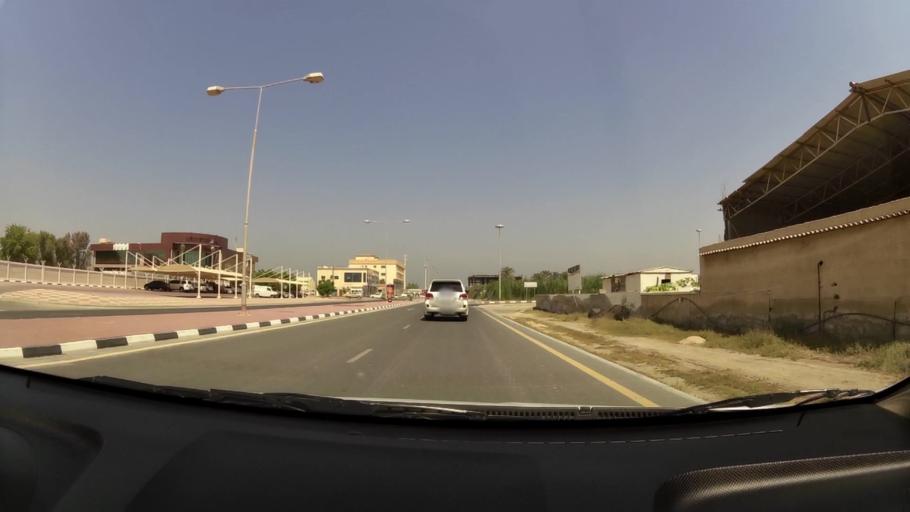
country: AE
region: Umm al Qaywayn
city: Umm al Qaywayn
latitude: 25.5562
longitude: 55.5522
